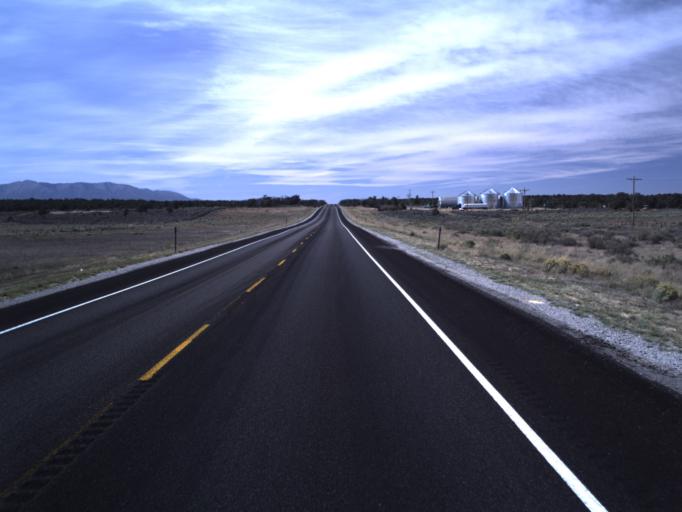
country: US
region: Colorado
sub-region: Dolores County
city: Dove Creek
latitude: 37.8333
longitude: -109.1004
